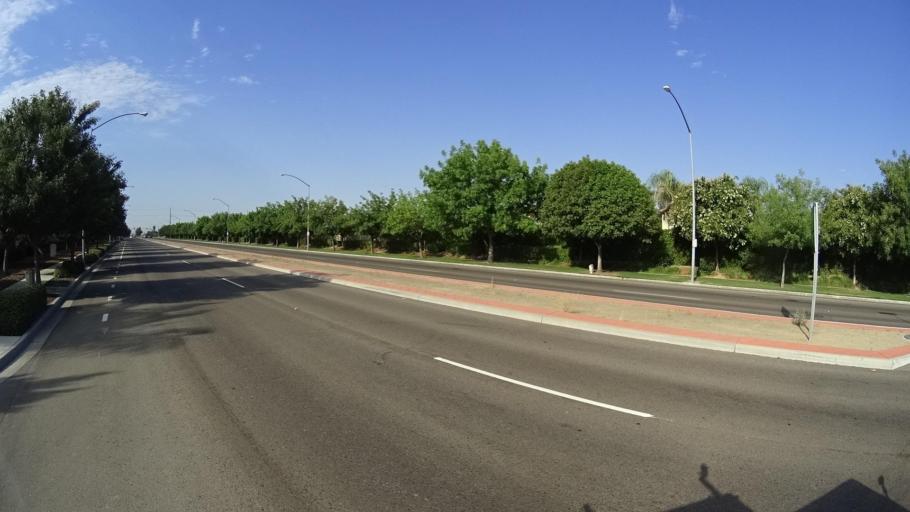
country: US
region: California
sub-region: Fresno County
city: Sunnyside
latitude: 36.7181
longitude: -119.6998
